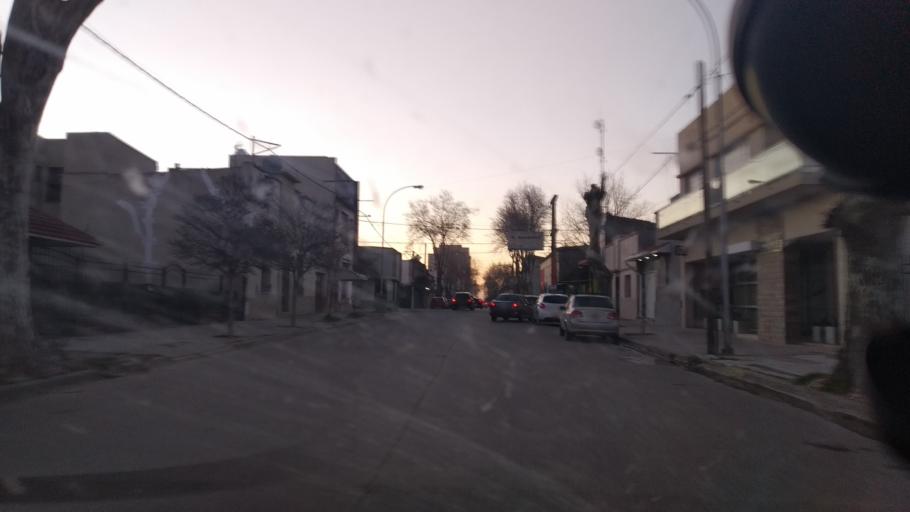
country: AR
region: Buenos Aires
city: Necochea
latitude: -38.5574
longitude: -58.7397
